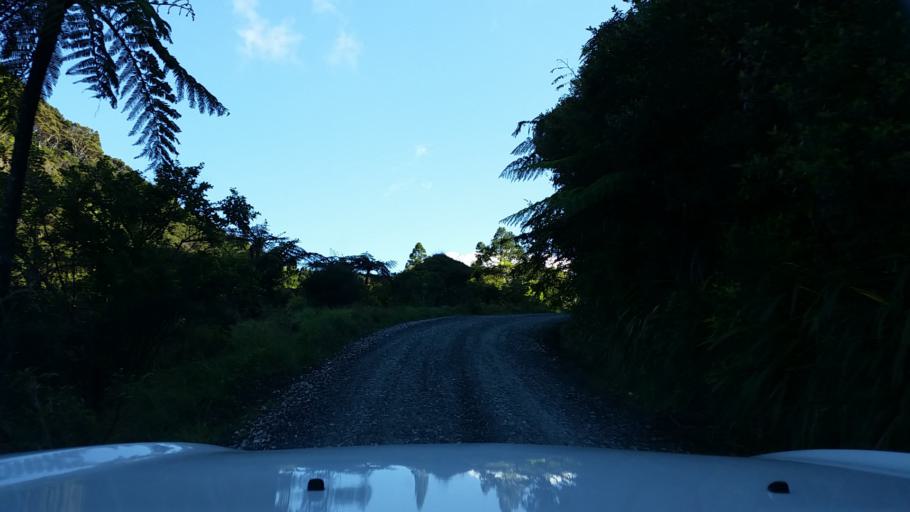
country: NZ
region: Auckland
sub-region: Auckland
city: Titirangi
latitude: -37.0182
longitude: 174.5375
